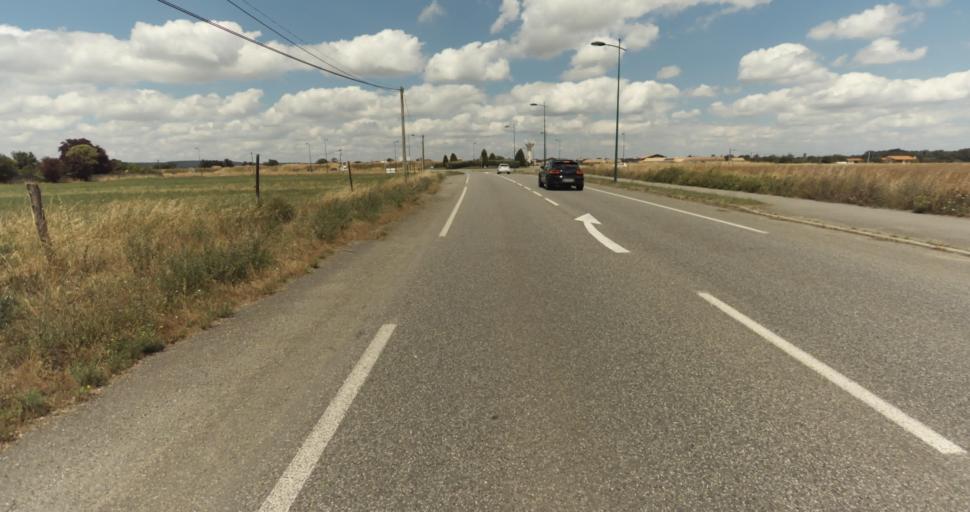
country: FR
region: Midi-Pyrenees
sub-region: Departement de la Haute-Garonne
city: Fontenilles
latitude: 43.5439
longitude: 1.1909
